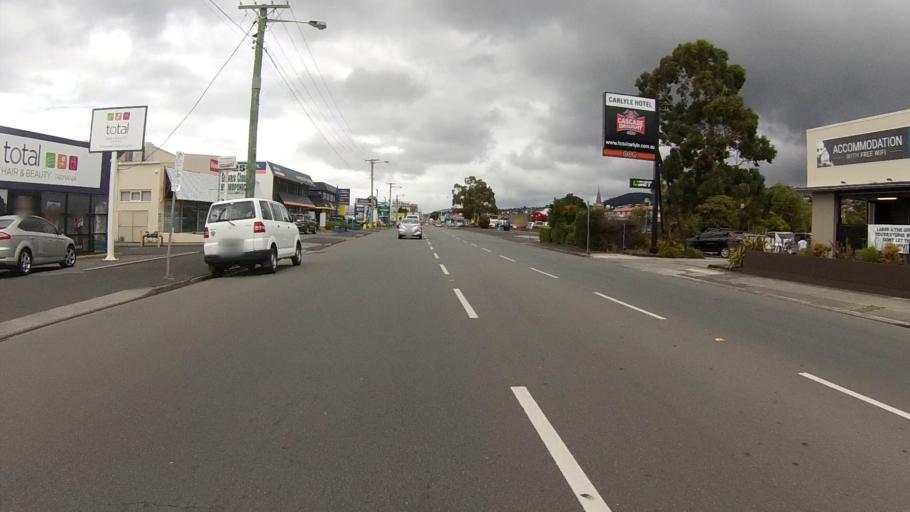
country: AU
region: Tasmania
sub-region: Glenorchy
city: Goodwood
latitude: -42.8383
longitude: 147.2890
